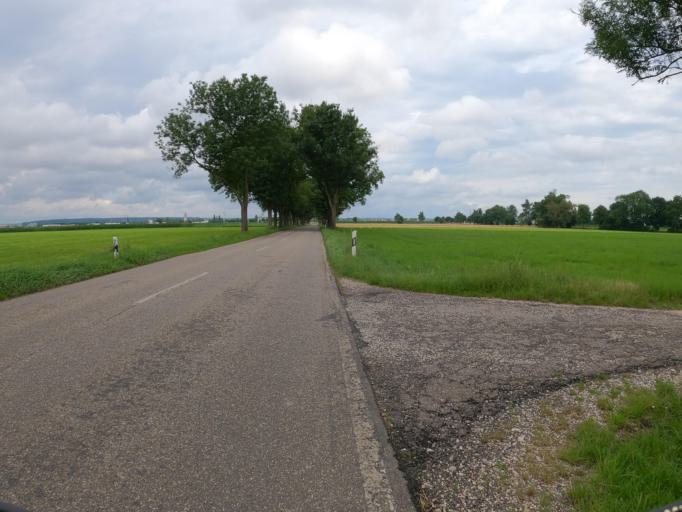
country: DE
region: Baden-Wuerttemberg
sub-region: Tuebingen Region
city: Langenau
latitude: 48.4839
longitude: 10.1417
